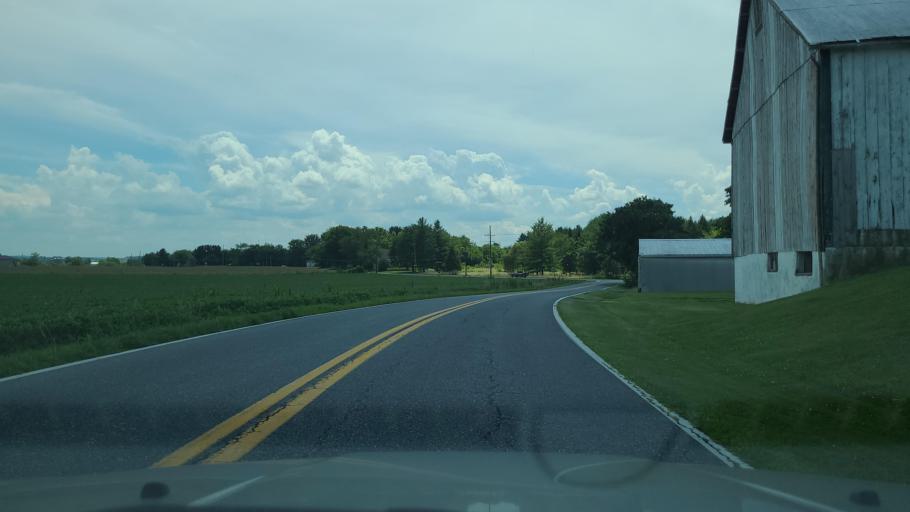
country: US
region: Maryland
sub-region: Frederick County
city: Thurmont
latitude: 39.5860
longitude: -77.3723
